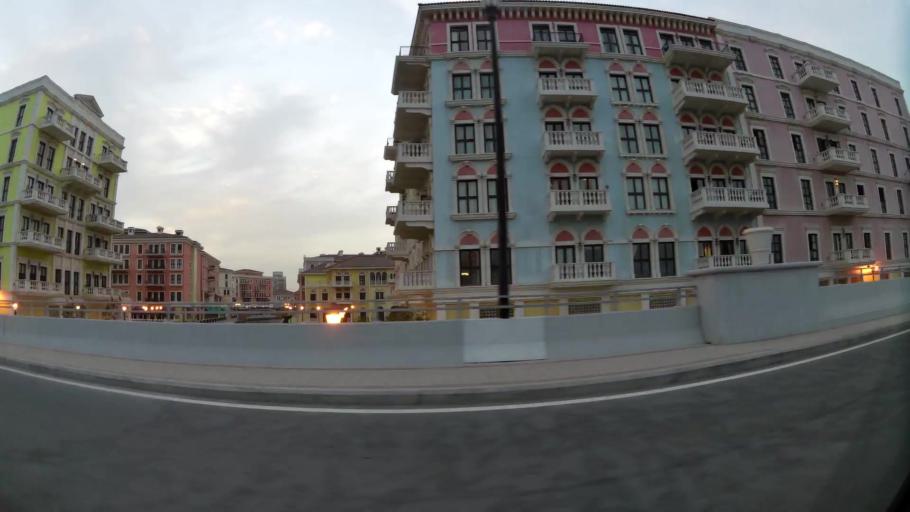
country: QA
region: Baladiyat ad Dawhah
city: Doha
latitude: 25.3777
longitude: 51.5466
